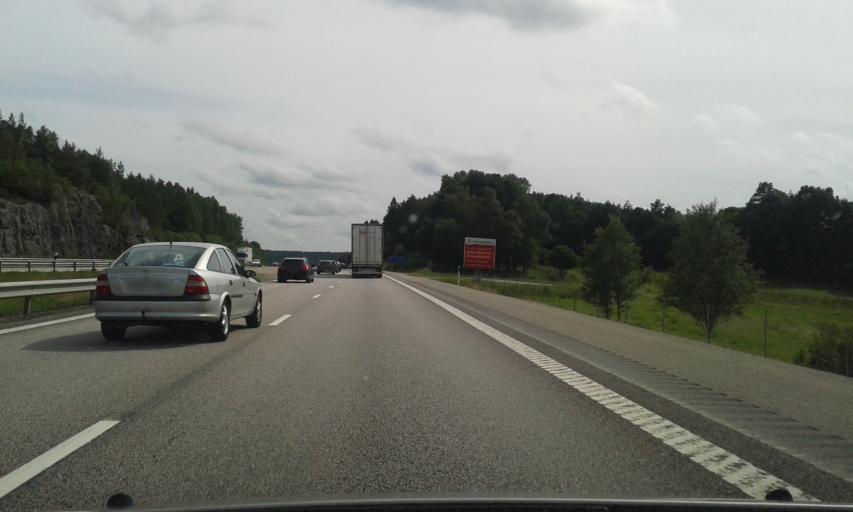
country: SE
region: Halland
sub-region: Kungsbacka Kommun
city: Frillesas
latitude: 57.3377
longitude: 12.2059
